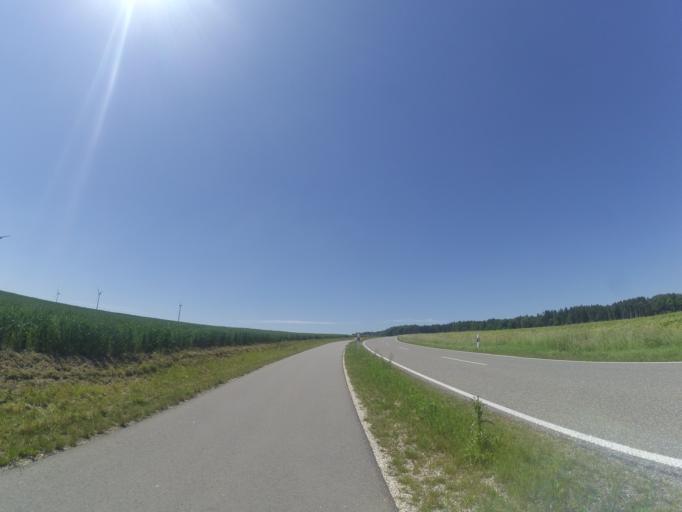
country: DE
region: Baden-Wuerttemberg
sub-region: Tuebingen Region
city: Lonsee
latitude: 48.4835
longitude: 9.8565
